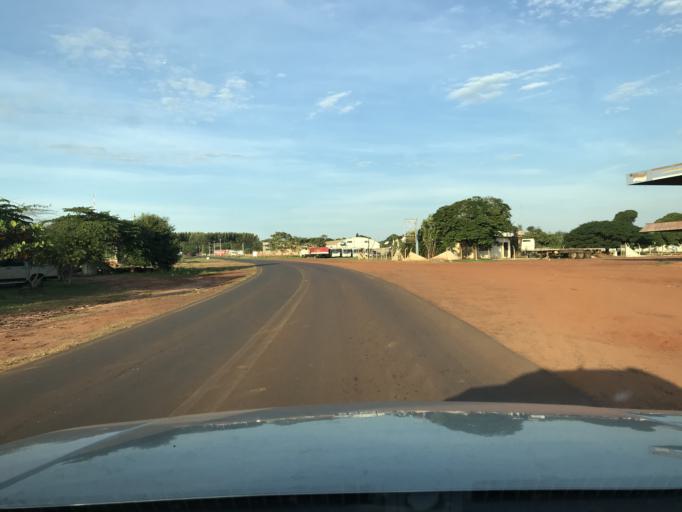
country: BR
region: Mato Grosso do Sul
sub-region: Iguatemi
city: Iguatemi
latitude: -23.6629
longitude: -54.5667
